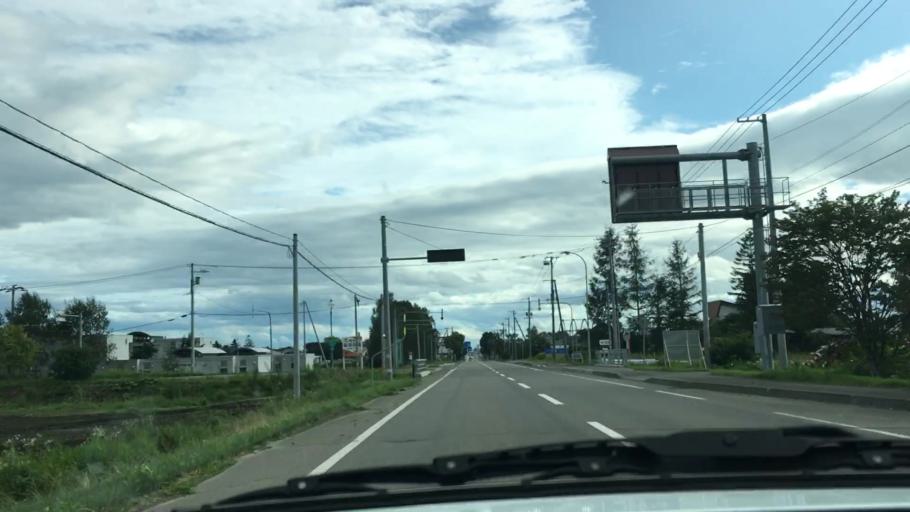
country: JP
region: Hokkaido
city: Otofuke
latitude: 43.2403
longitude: 143.2968
